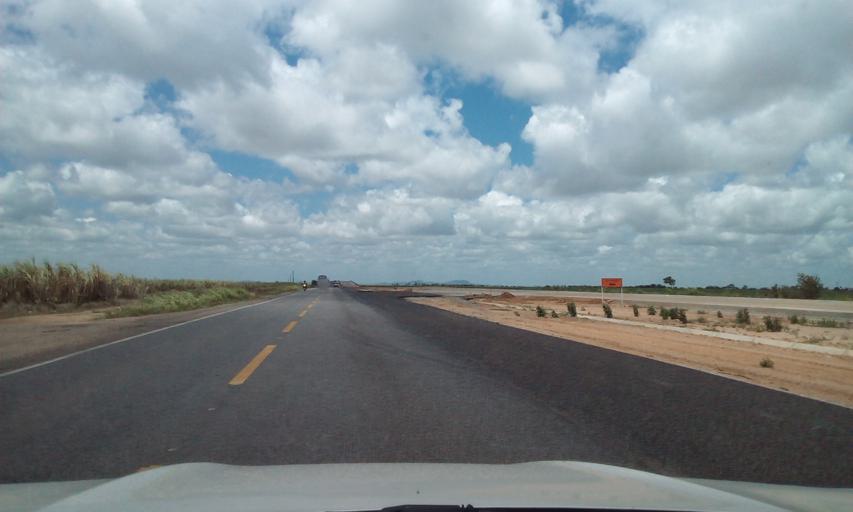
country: BR
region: Alagoas
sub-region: Sao Miguel Dos Campos
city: Sao Miguel dos Campos
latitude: -9.8755
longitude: -36.1381
